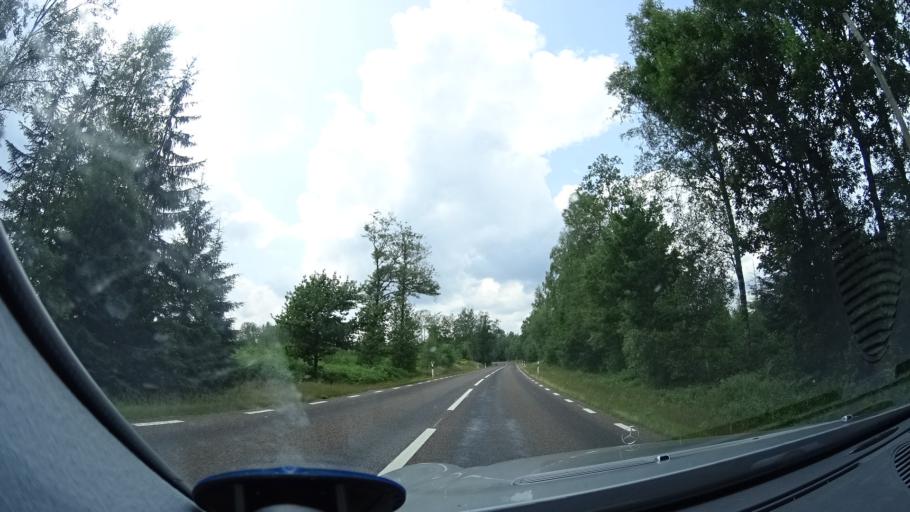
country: SE
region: Kalmar
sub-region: Emmaboda Kommun
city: Emmaboda
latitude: 56.6290
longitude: 15.6316
